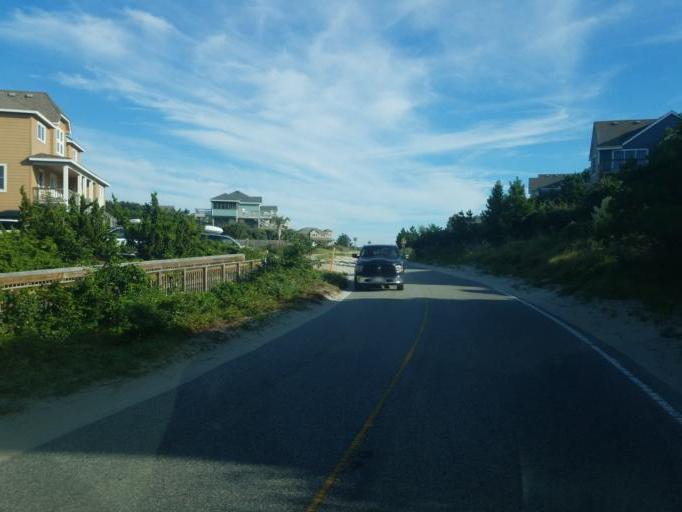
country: US
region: North Carolina
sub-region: Currituck County
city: Currituck
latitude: 36.3926
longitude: -75.8298
